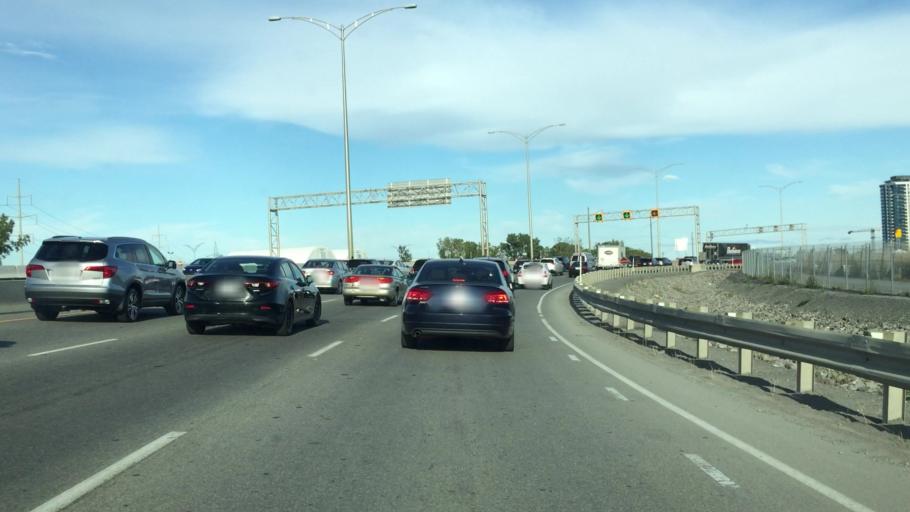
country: CA
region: Quebec
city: Westmount
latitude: 45.4735
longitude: -73.5523
